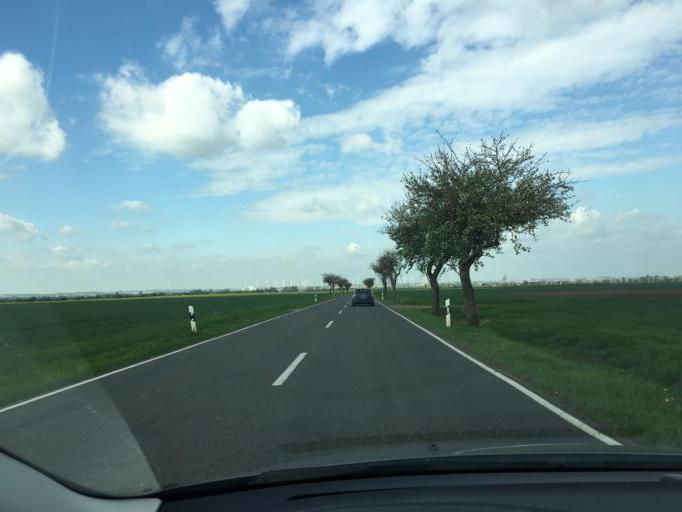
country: DE
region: Saxony-Anhalt
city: Peissen
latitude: 51.7244
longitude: 11.7505
